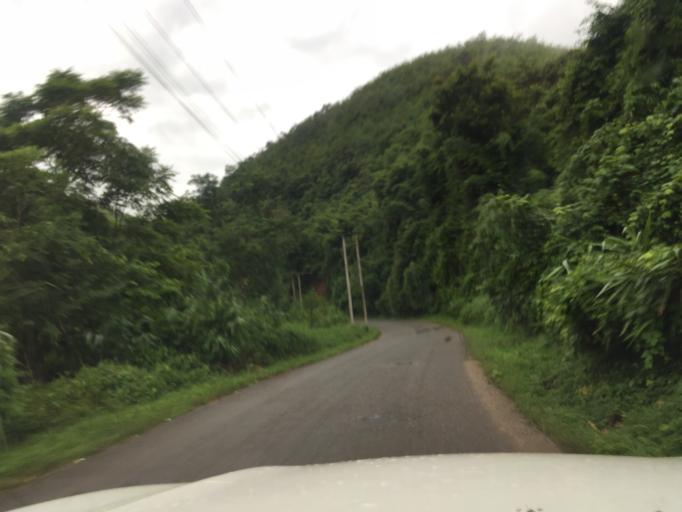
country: LA
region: Oudomxai
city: Muang La
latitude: 20.9422
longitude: 102.2073
